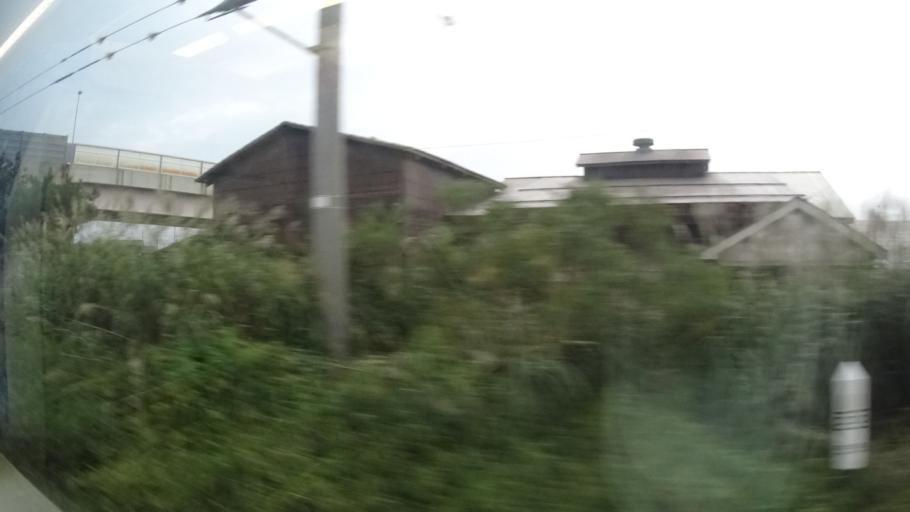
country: JP
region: Niigata
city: Murakami
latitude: 38.1859
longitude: 139.4597
